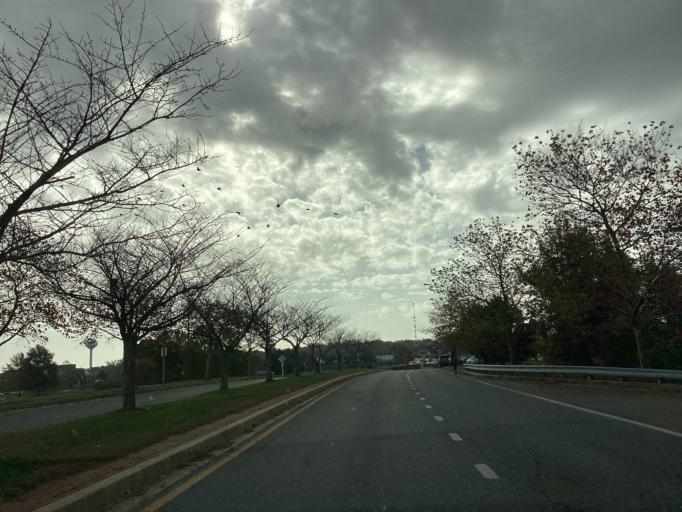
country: US
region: Maryland
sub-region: Somerset County
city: Princess Anne
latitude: 38.2141
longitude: -75.6866
